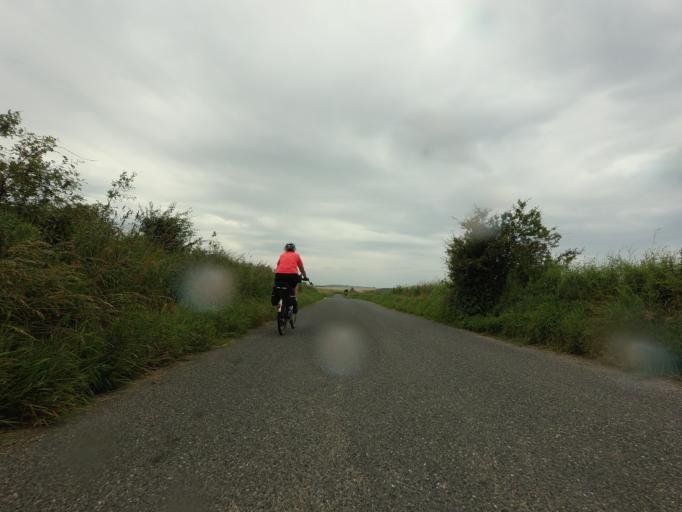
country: GB
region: Scotland
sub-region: Aberdeenshire
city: Whitehills
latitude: 57.6729
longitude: -2.6366
